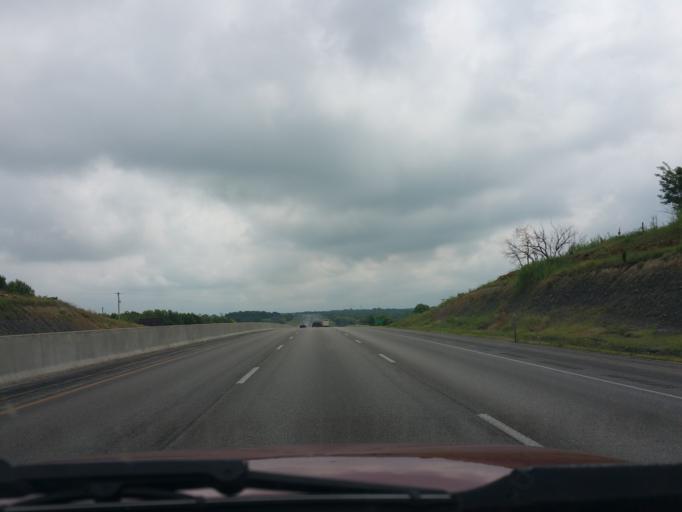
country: US
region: Kansas
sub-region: Shawnee County
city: Topeka
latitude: 39.0266
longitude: -95.5558
